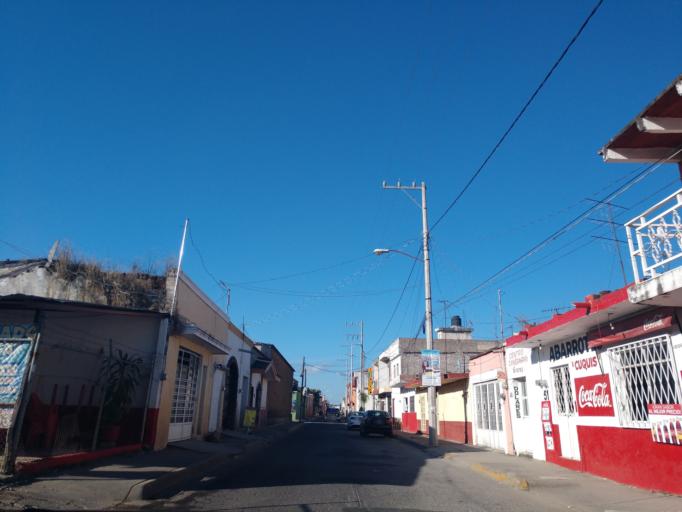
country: MX
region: Nayarit
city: Xalisco
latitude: 21.4415
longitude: -104.8991
